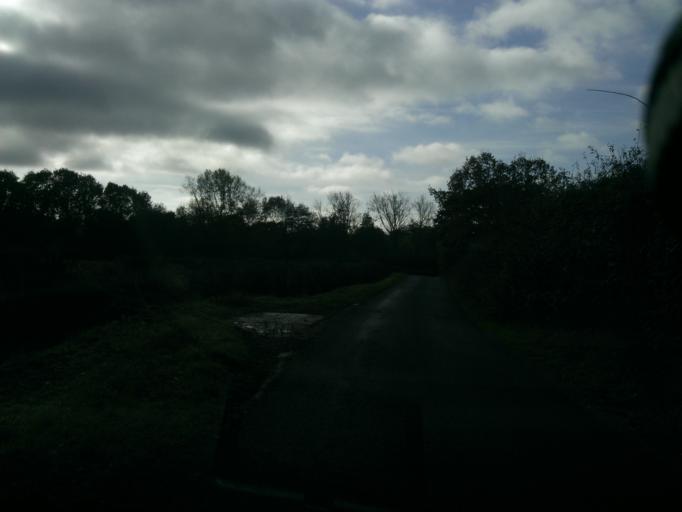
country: GB
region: England
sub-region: Essex
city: Braintree
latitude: 51.8423
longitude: 0.4673
